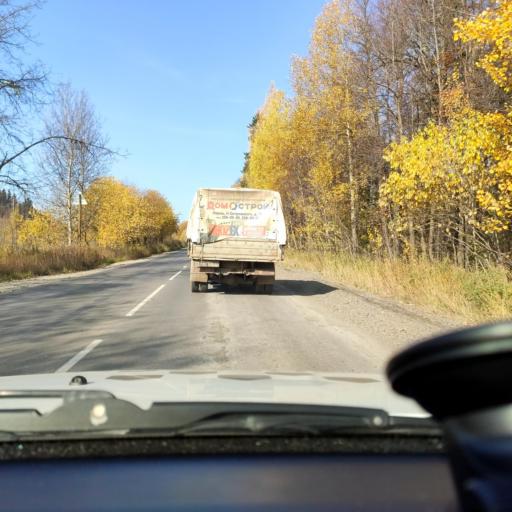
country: RU
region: Perm
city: Ferma
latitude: 57.9683
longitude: 56.3511
